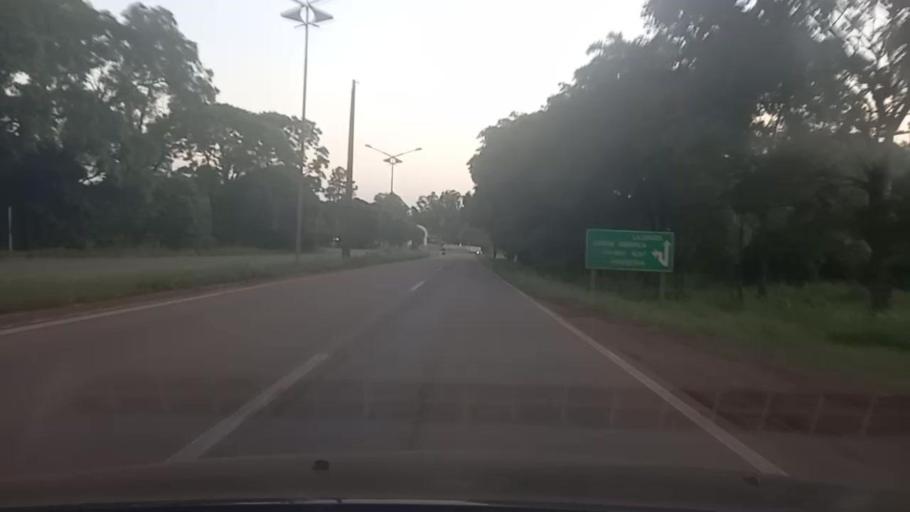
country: BR
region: Rio Grande do Sul
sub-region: Passo Fundo
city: Passo Fundo
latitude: -28.2873
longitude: -52.4542
